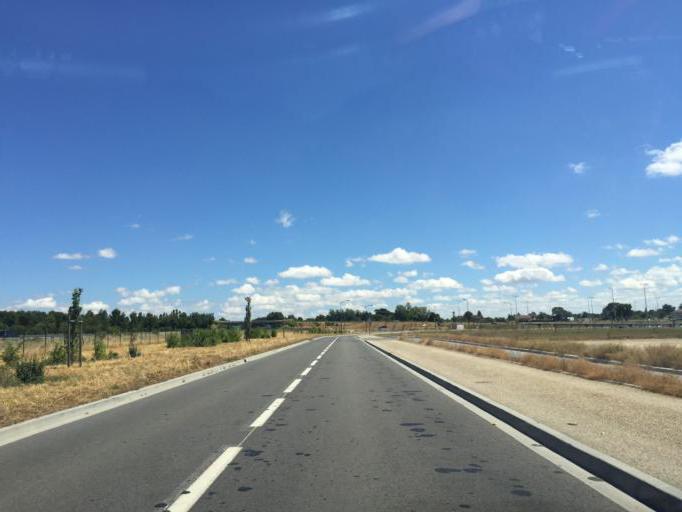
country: FR
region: Auvergne
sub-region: Departement de l'Allier
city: Avermes
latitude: 46.5907
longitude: 3.3275
